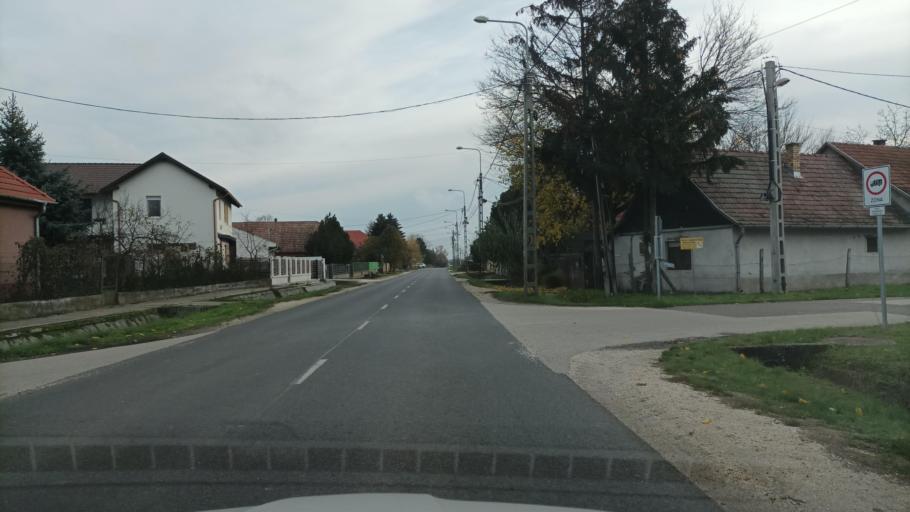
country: HU
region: Pest
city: Ocsa
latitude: 47.3005
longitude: 19.2204
